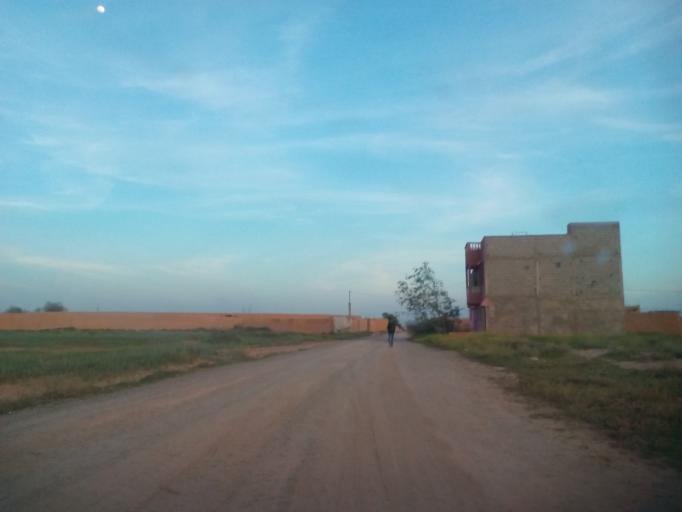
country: MA
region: Marrakech-Tensift-Al Haouz
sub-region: Marrakech
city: Marrakesh
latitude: 31.6277
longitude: -8.2873
